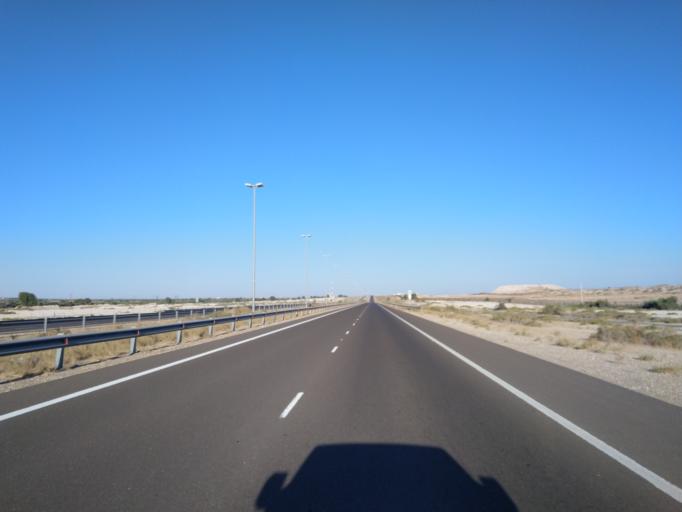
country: OM
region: Al Buraimi
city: Al Buraymi
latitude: 24.5306
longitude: 55.5680
